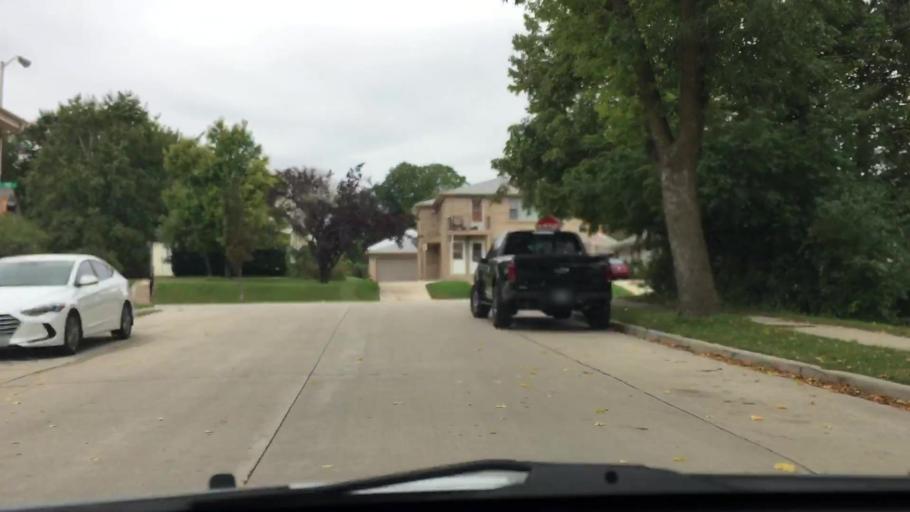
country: US
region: Wisconsin
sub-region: Milwaukee County
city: West Allis
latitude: 43.0141
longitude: -88.0267
